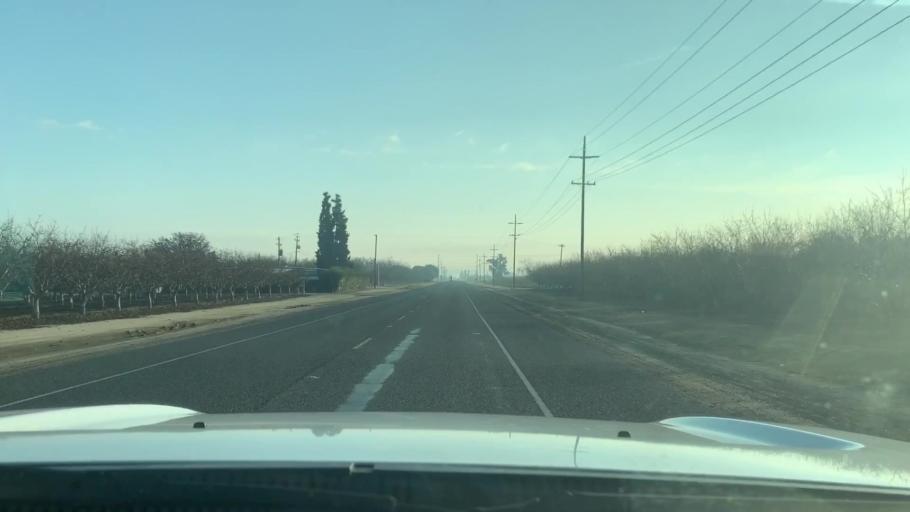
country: US
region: California
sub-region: Kern County
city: Wasco
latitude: 35.6015
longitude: -119.3733
